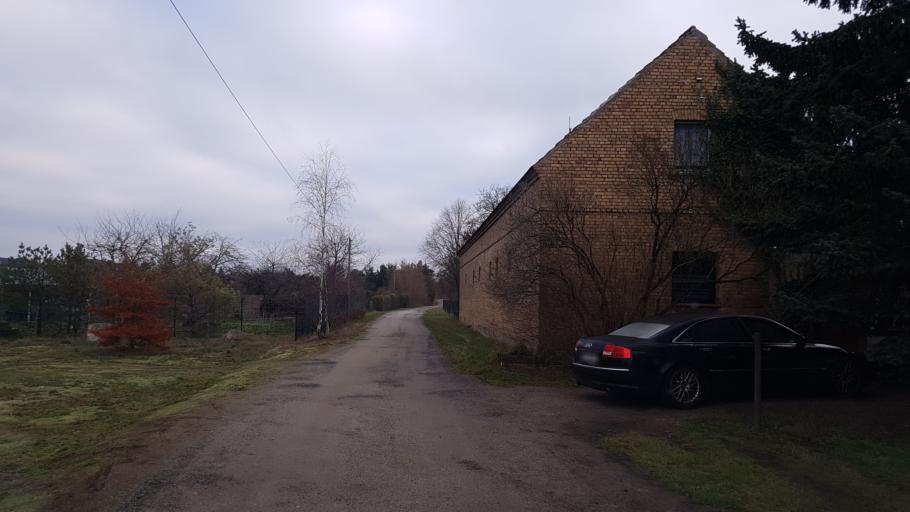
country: DE
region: Brandenburg
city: Sallgast
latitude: 51.5871
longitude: 13.8173
